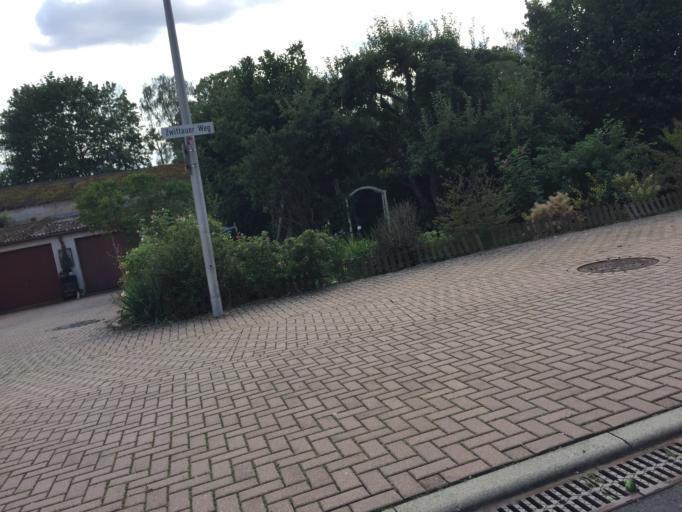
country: DE
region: Hesse
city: Schwalmstadt
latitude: 50.9034
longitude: 9.2726
